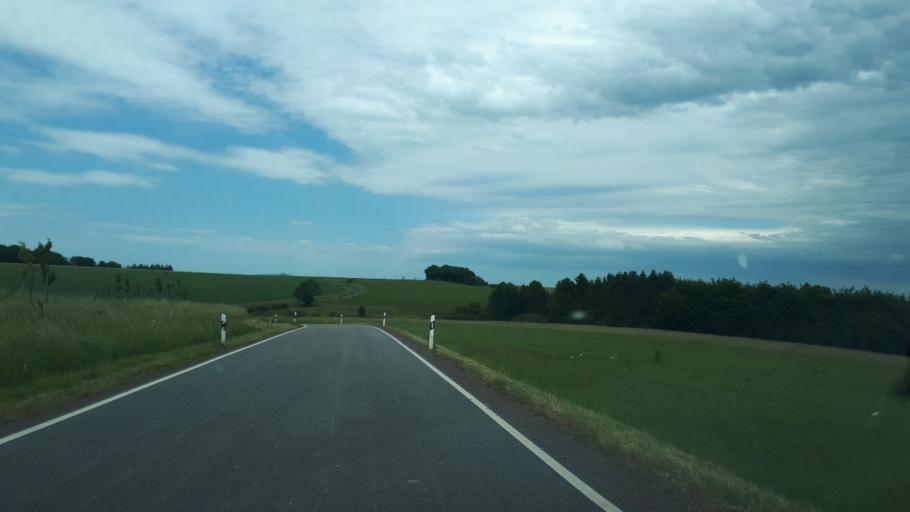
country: DE
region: Rheinland-Pfalz
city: Immerath
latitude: 50.1305
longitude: 6.9499
